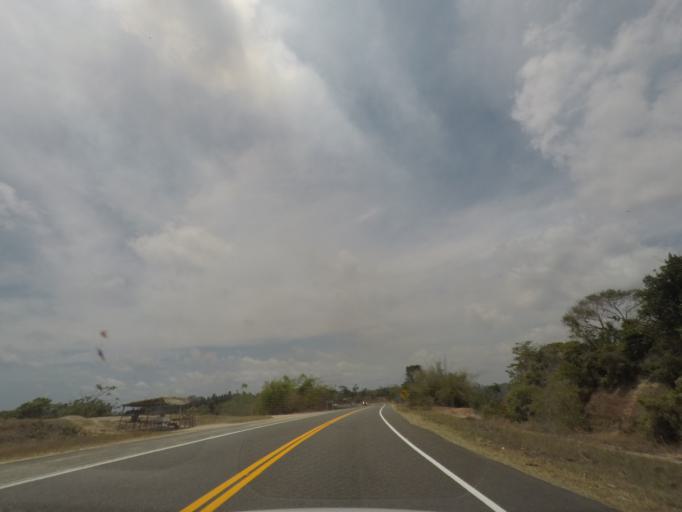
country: BR
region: Bahia
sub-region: Conde
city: Conde
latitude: -11.7581
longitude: -37.5883
